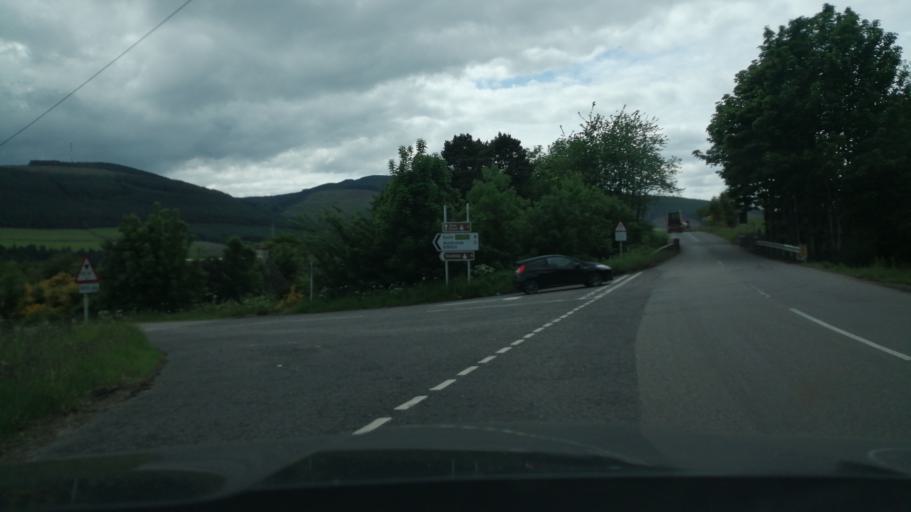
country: GB
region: Scotland
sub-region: Moray
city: Rothes
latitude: 57.5543
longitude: -3.1533
